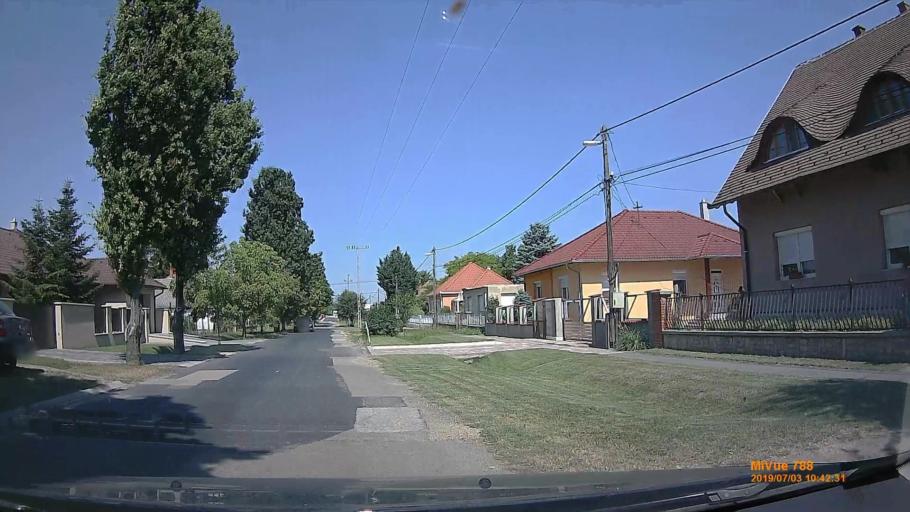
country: HU
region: Gyor-Moson-Sopron
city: Gyorujbarat
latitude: 47.6383
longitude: 17.6127
